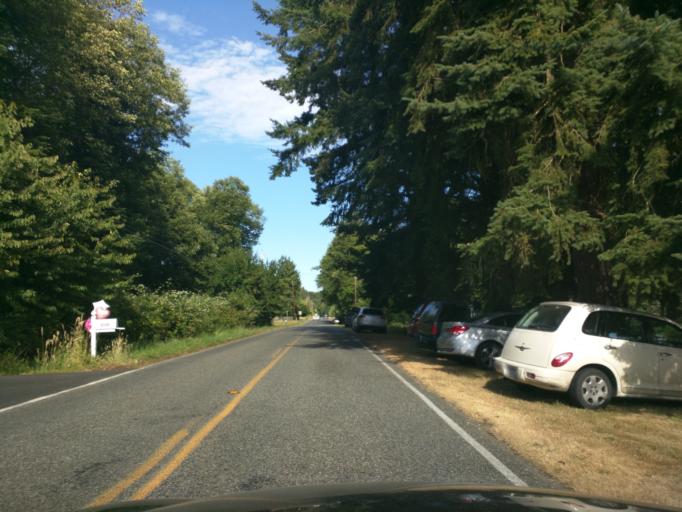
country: US
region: Washington
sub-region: Whatcom County
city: Blaine
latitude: 48.9939
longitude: -122.7078
